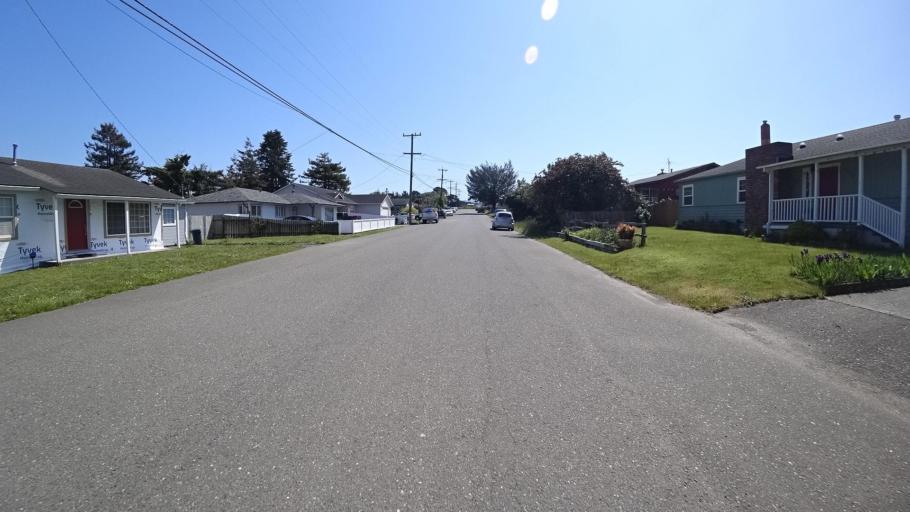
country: US
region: California
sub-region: Humboldt County
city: Fortuna
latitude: 40.5650
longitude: -124.1340
